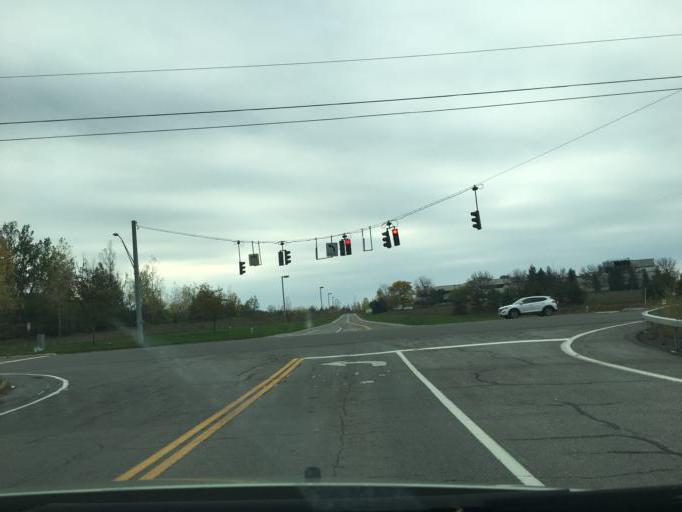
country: US
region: New York
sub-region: Ontario County
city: Canandaigua
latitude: 42.9242
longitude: -77.3083
